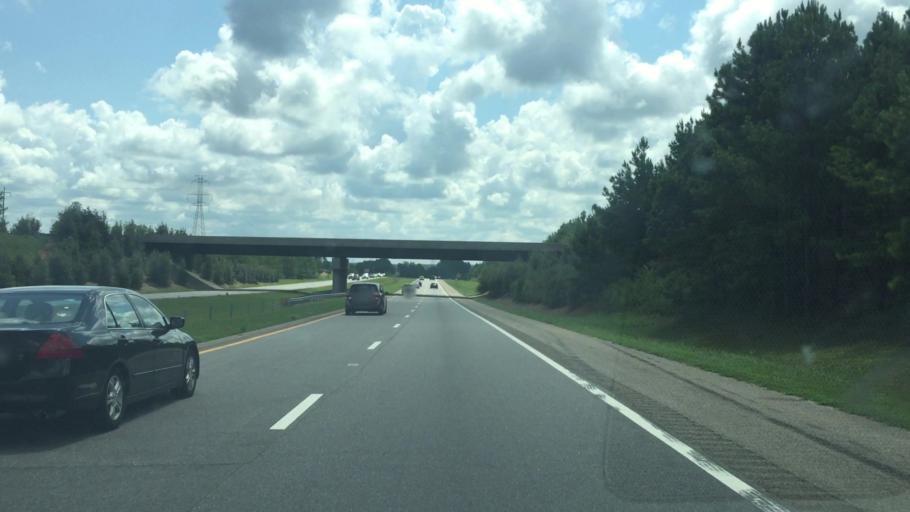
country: US
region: North Carolina
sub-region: Richmond County
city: Cordova
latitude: 34.9321
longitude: -79.8327
